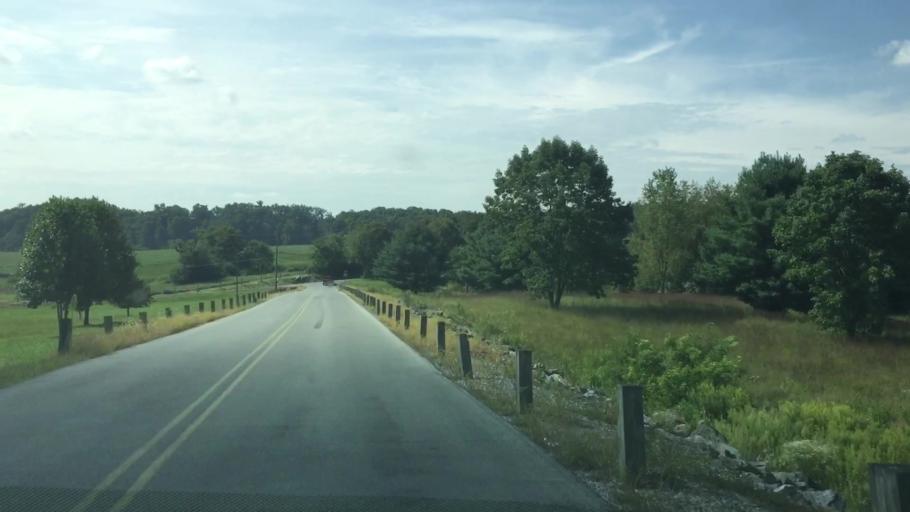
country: US
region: Tennessee
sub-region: Sullivan County
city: Fairmount
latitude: 36.5824
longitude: -82.0503
